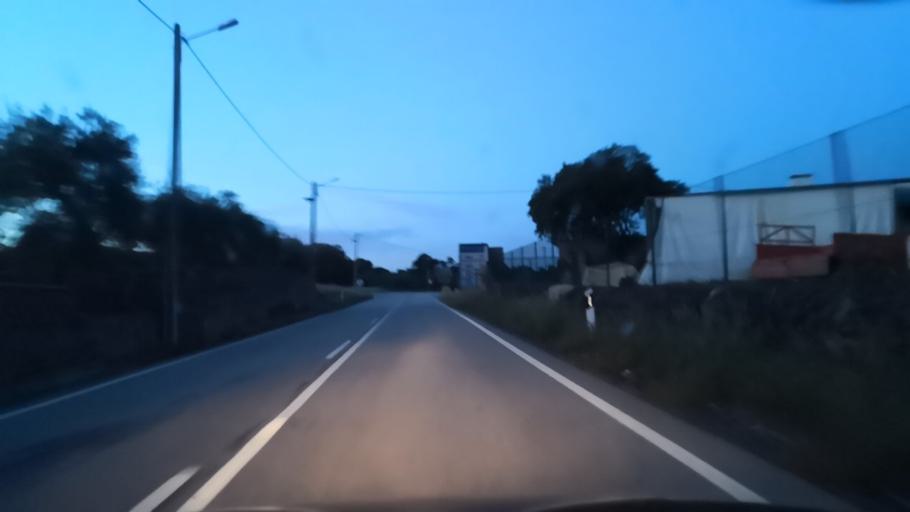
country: ES
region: Extremadura
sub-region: Provincia de Caceres
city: Piedras Albas
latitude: 39.8341
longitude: -6.9751
